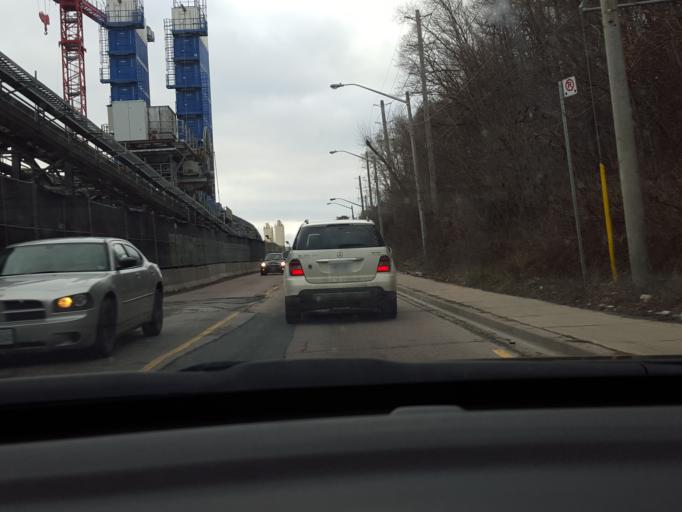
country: CA
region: Ontario
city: Toronto
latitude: 43.7158
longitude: -79.3545
